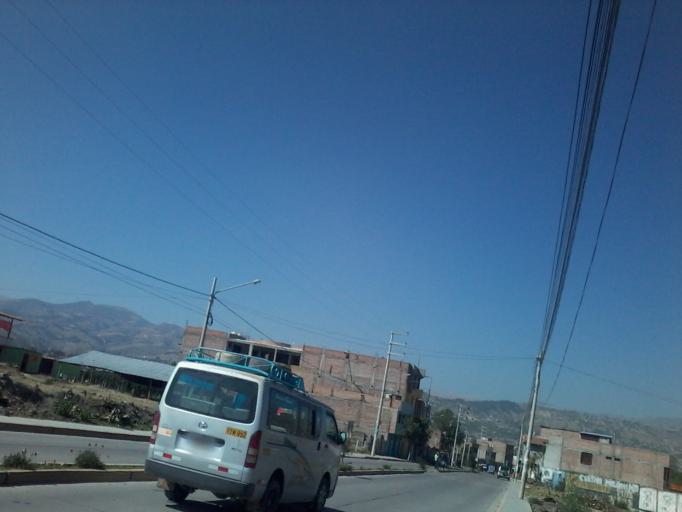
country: PE
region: Ayacucho
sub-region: Provincia de Huamanga
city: Ayacucho
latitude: -13.1562
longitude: -74.2075
